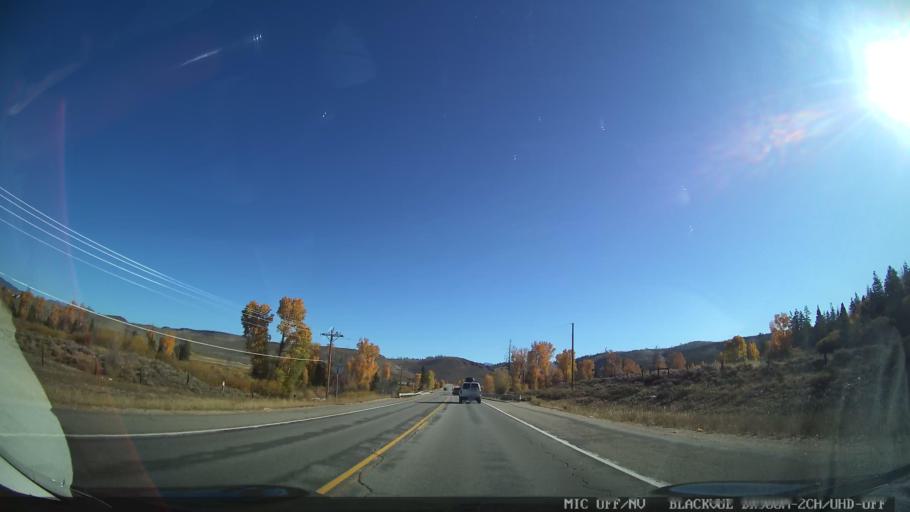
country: US
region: Colorado
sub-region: Grand County
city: Granby
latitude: 40.1176
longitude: -105.9084
